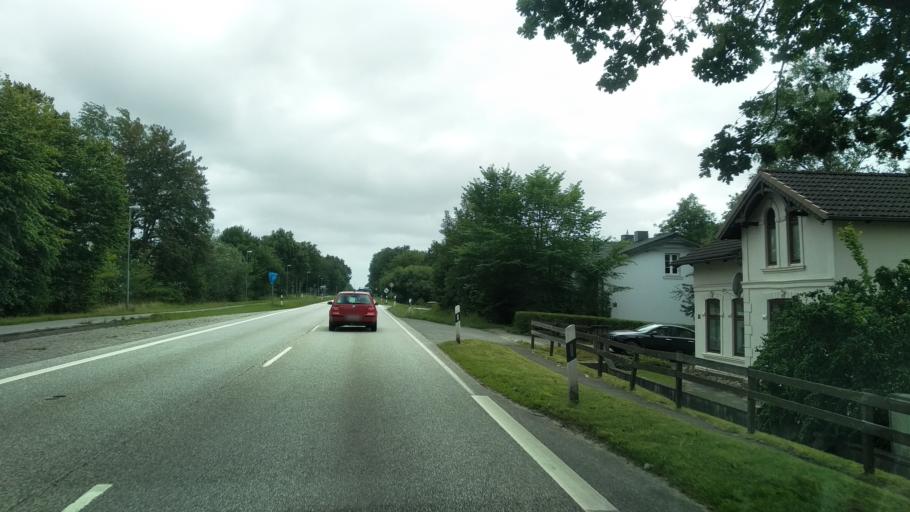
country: DE
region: Schleswig-Holstein
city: Oeversee
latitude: 54.7022
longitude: 9.4366
